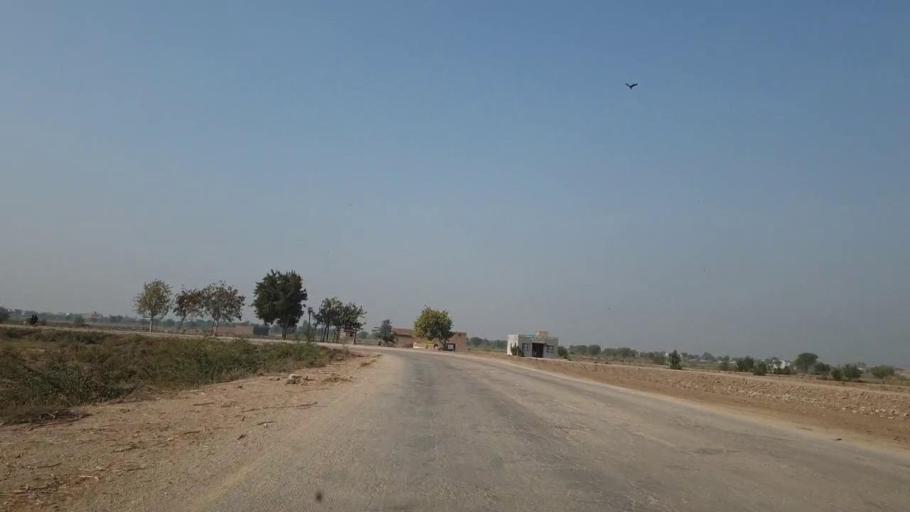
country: PK
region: Sindh
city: Mirpur Khas
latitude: 25.5398
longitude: 69.0453
